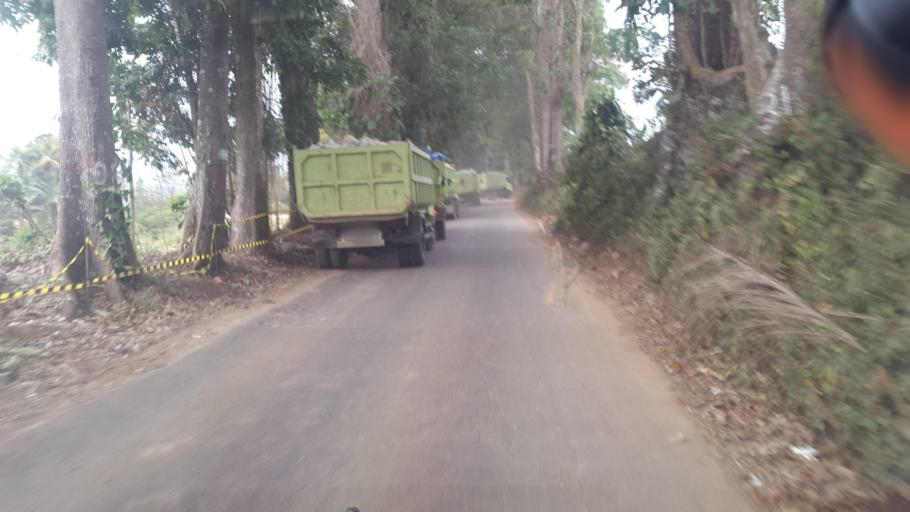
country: ID
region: West Java
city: Cicurug
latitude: -6.7727
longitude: 106.8046
